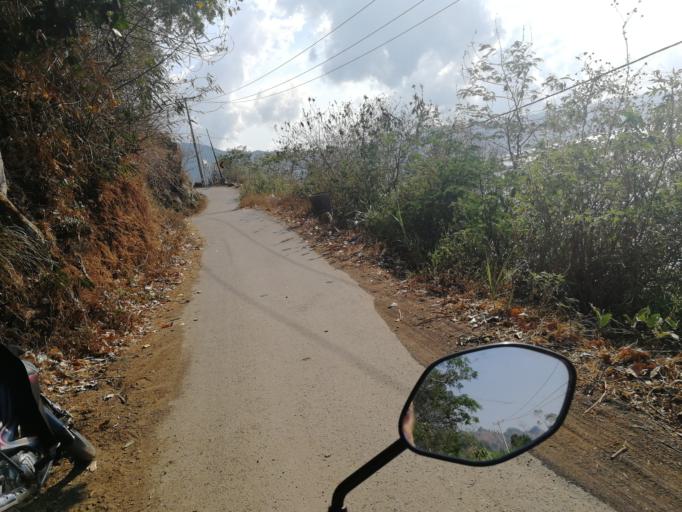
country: ID
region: Bali
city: Banjar Trunyan
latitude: -8.2676
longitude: 115.4194
